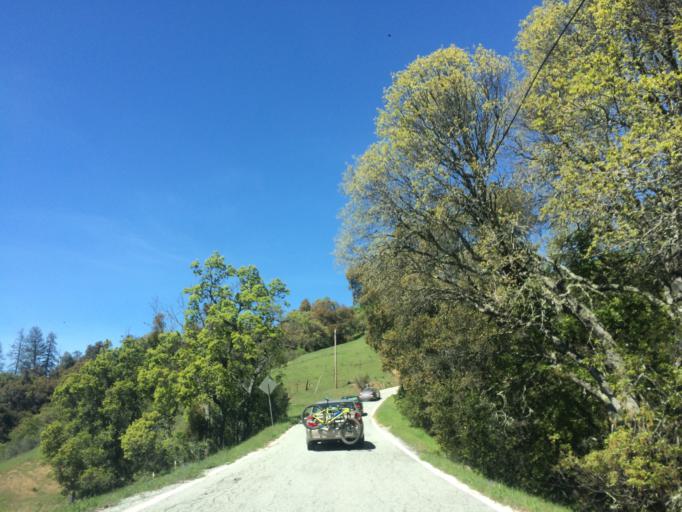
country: US
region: California
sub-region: Santa Clara County
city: Morgan Hill
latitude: 37.1884
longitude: -121.5542
